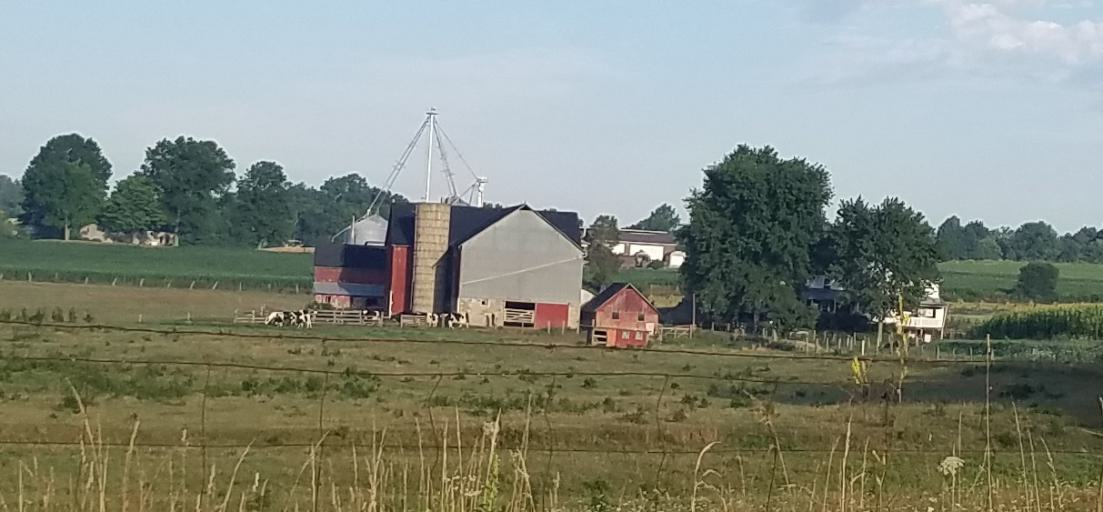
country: US
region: Ohio
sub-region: Wayne County
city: Apple Creek
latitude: 40.7278
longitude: -81.8770
